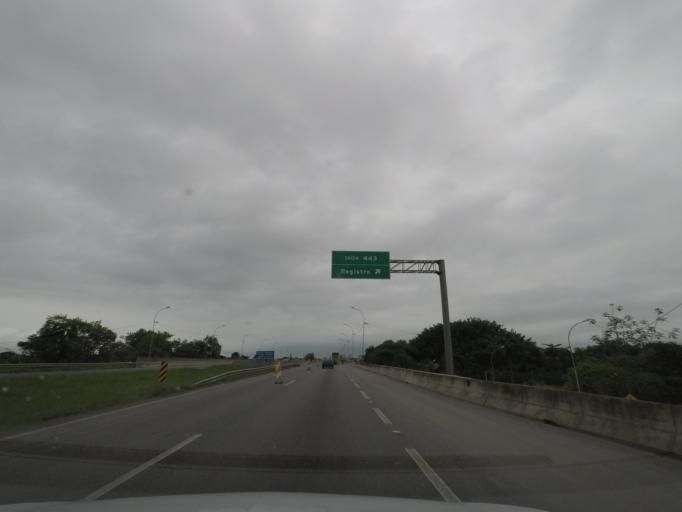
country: BR
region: Sao Paulo
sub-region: Registro
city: Registro
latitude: -24.4872
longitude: -47.8345
